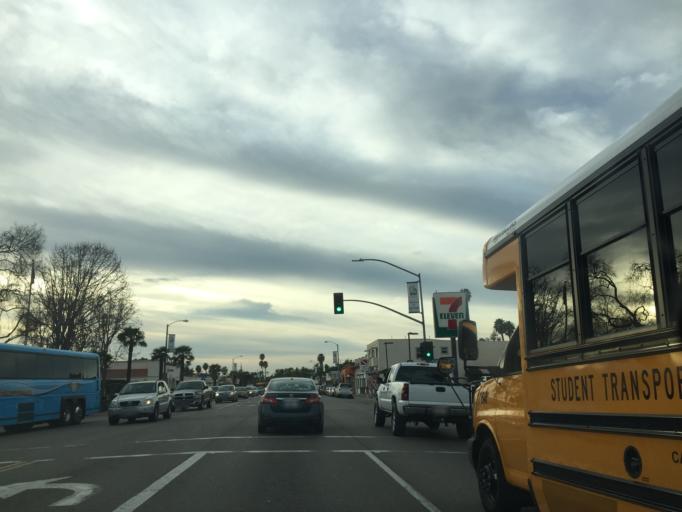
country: US
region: California
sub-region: Santa Barbara County
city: Goleta
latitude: 34.4359
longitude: -119.8263
